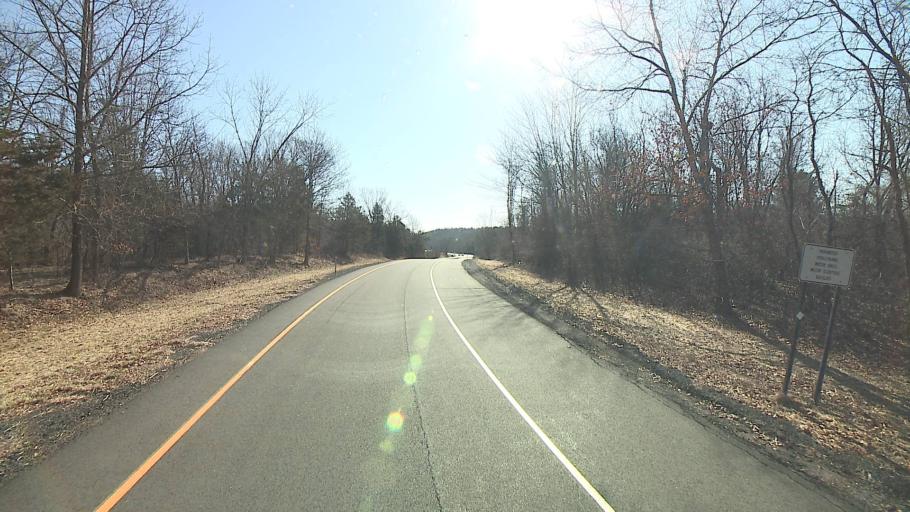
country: US
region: Connecticut
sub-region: Hartford County
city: Terramuggus
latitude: 41.6664
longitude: -72.5335
